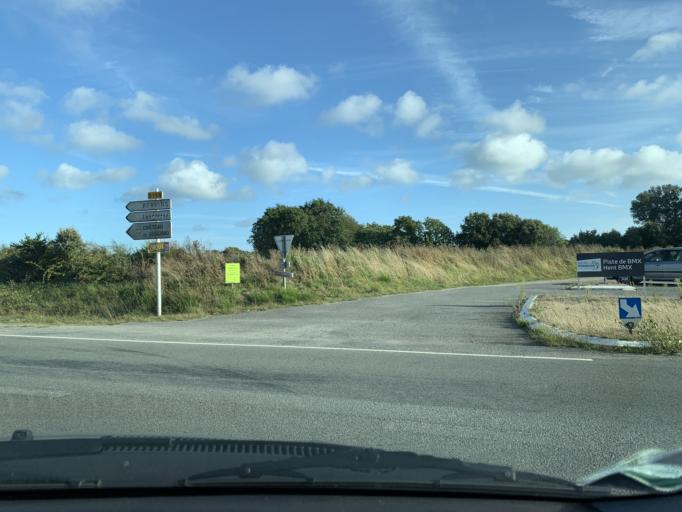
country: FR
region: Brittany
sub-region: Departement du Morbihan
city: Sarzeau
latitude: 47.5271
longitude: -2.7518
